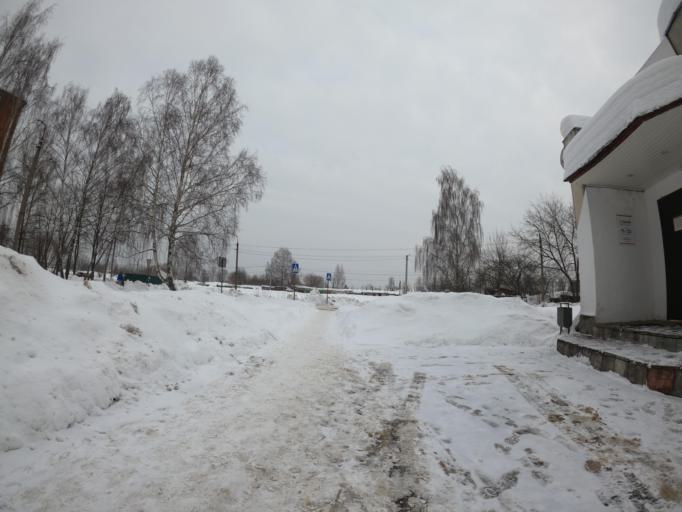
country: RU
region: Moskovskaya
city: Elektrogorsk
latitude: 55.8747
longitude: 38.7863
